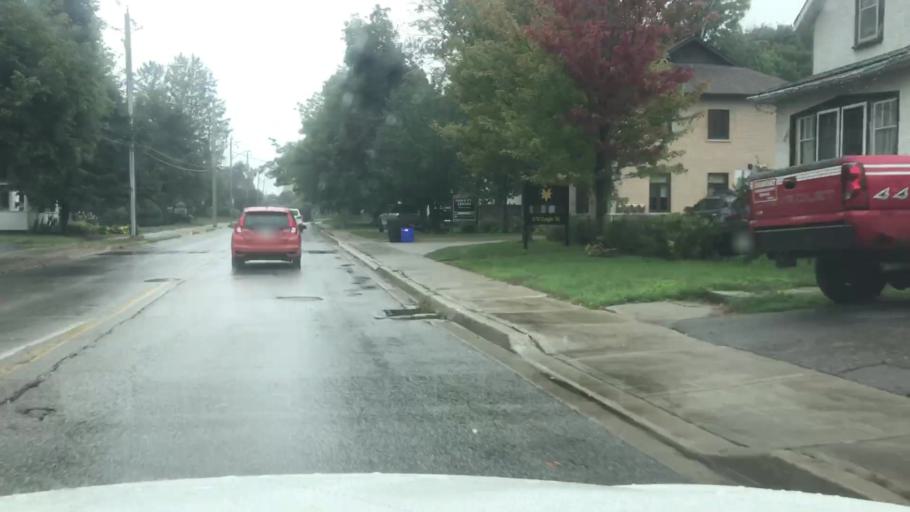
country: CA
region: Ontario
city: Newmarket
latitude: 44.0490
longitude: -79.4617
